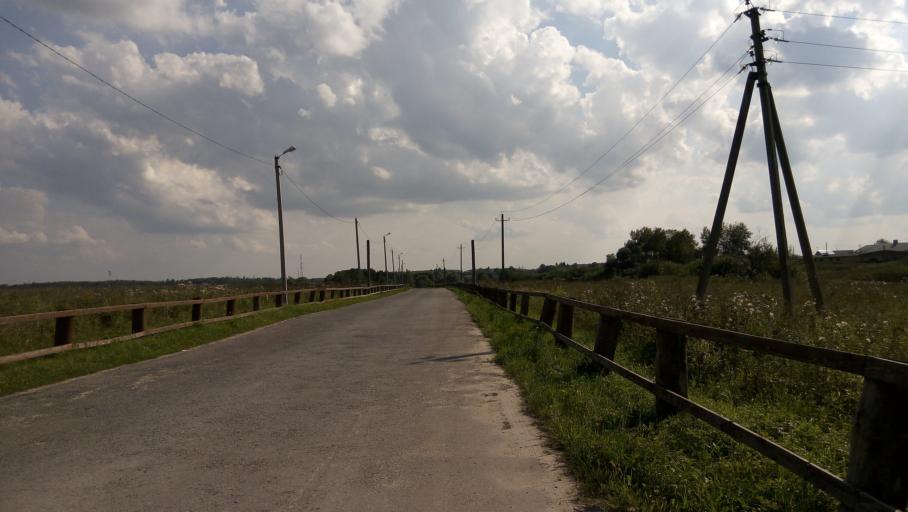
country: RU
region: Moskovskaya
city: Proletarskiy
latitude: 55.0446
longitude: 37.4140
